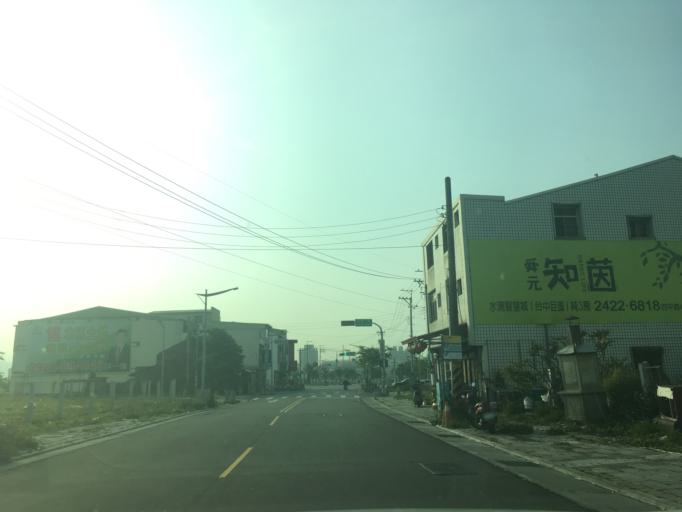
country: TW
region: Taiwan
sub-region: Taichung City
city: Taichung
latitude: 24.1986
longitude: 120.6784
